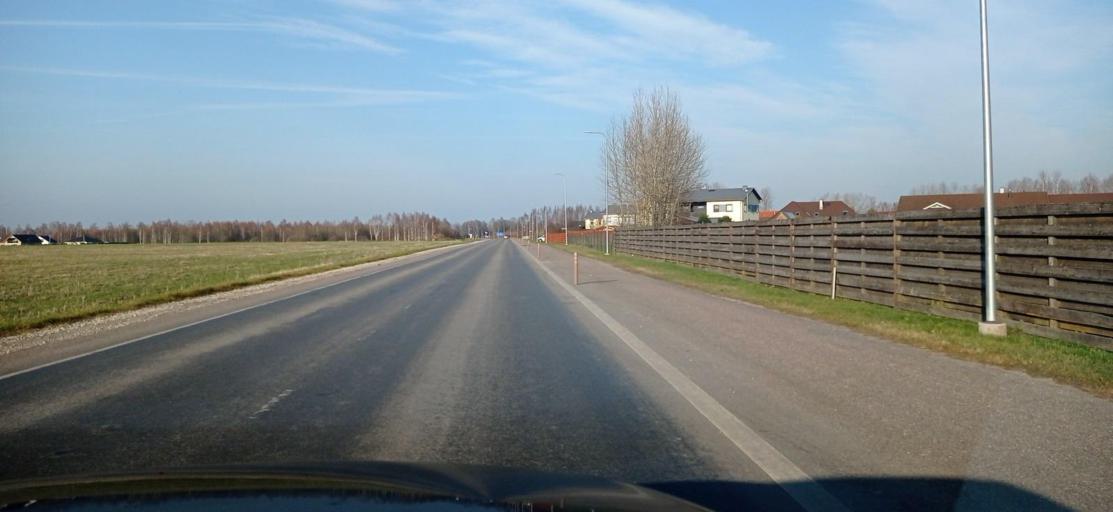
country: EE
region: Tartu
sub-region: Tartu linn
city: Tartu
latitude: 58.4041
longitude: 26.7220
